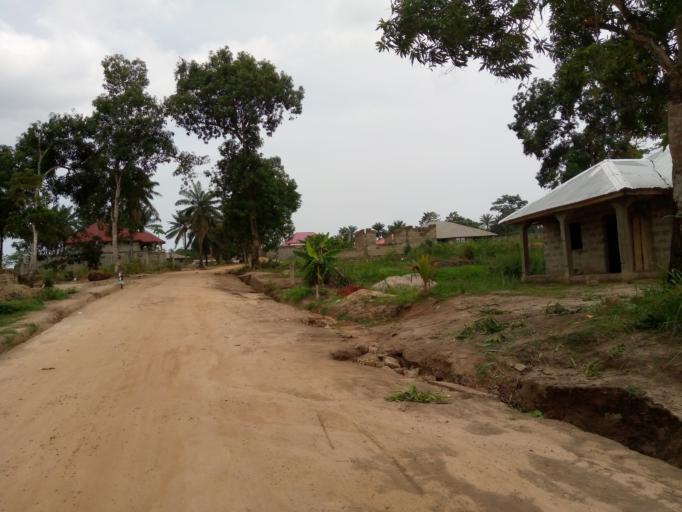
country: SL
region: Western Area
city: Waterloo
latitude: 8.3402
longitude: -13.0160
